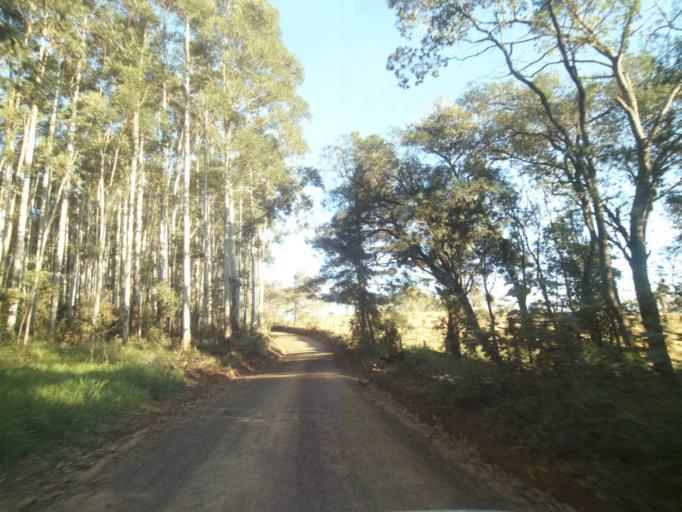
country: BR
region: Parana
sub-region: Telemaco Borba
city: Telemaco Borba
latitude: -24.5116
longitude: -50.6040
